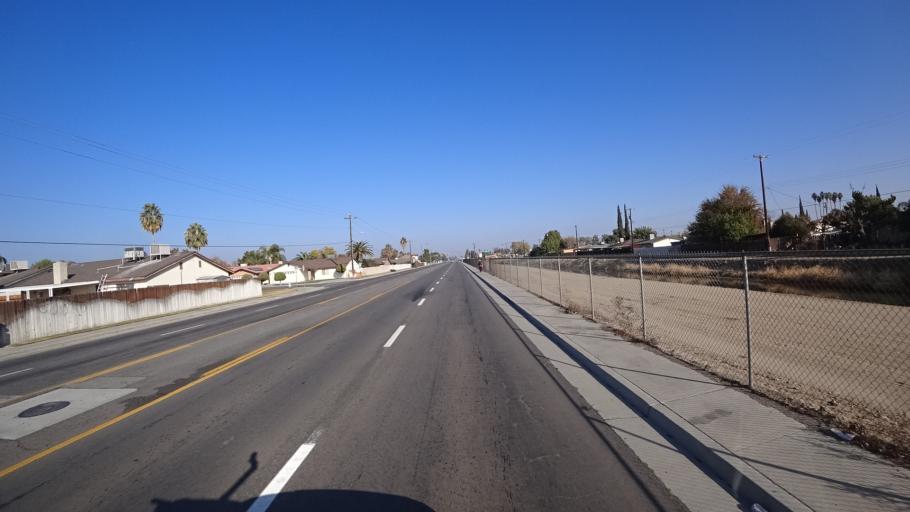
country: US
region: California
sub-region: Kern County
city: Greenfield
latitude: 35.3008
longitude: -119.0212
